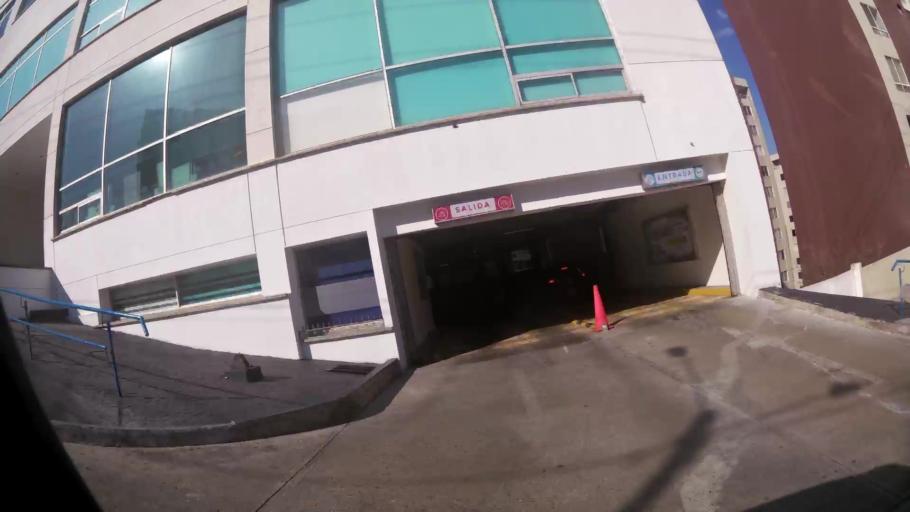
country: CO
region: Atlantico
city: Barranquilla
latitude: 11.0039
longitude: -74.8350
